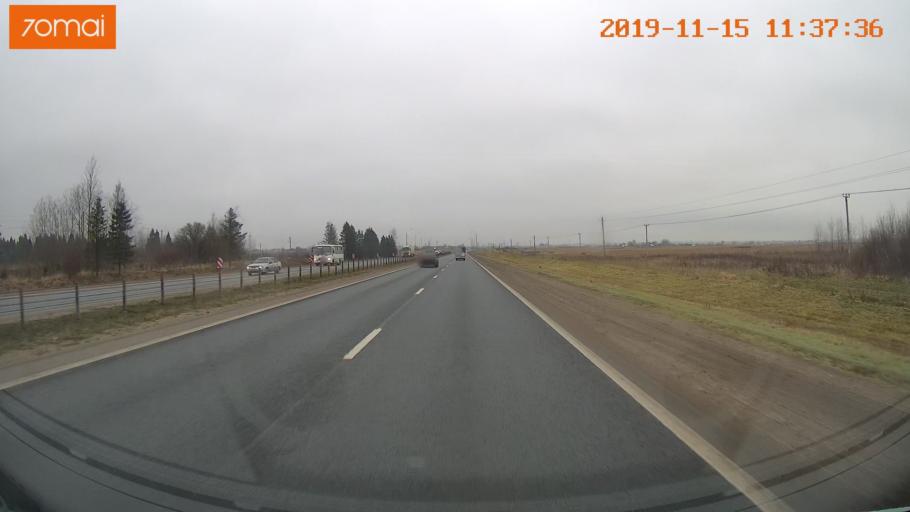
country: RU
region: Vologda
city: Molochnoye
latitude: 59.2063
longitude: 39.6763
